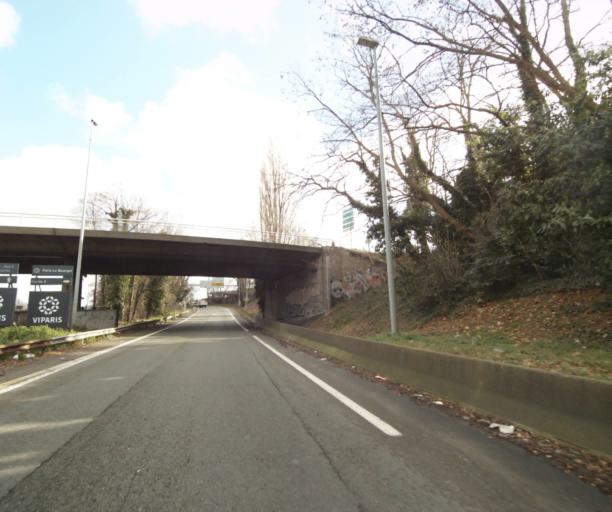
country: FR
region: Ile-de-France
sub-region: Departement de Seine-Saint-Denis
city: Le Bourget
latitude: 48.9414
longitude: 2.4292
